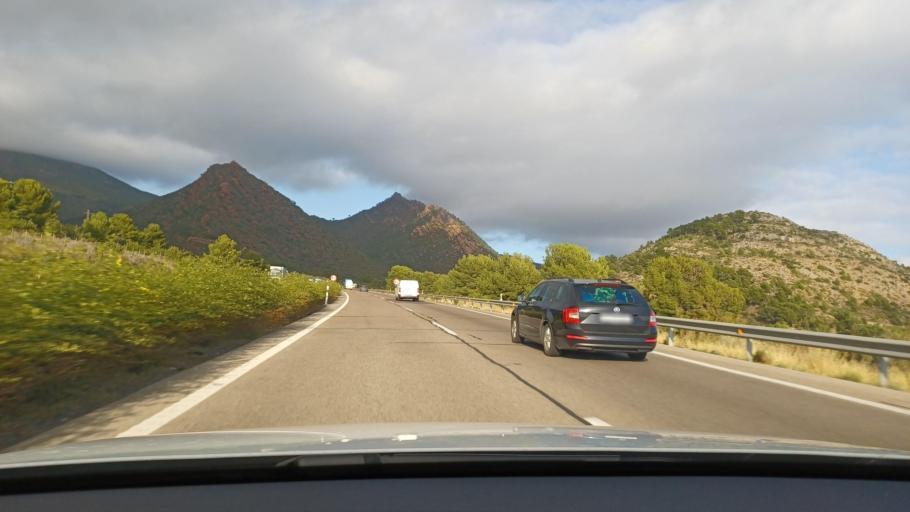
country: ES
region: Valencia
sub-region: Provincia de Castello
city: Benicassim
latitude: 40.0536
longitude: 0.0415
